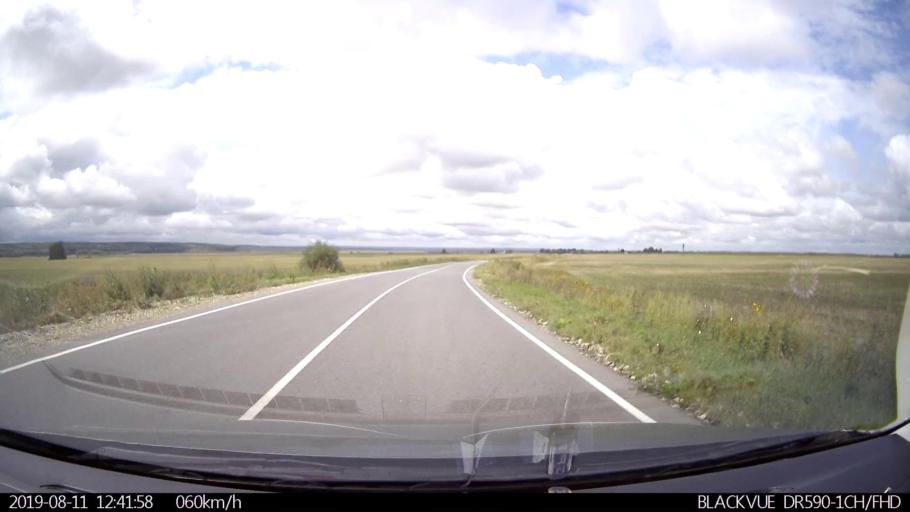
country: RU
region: Ulyanovsk
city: Ignatovka
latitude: 53.8426
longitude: 47.7571
